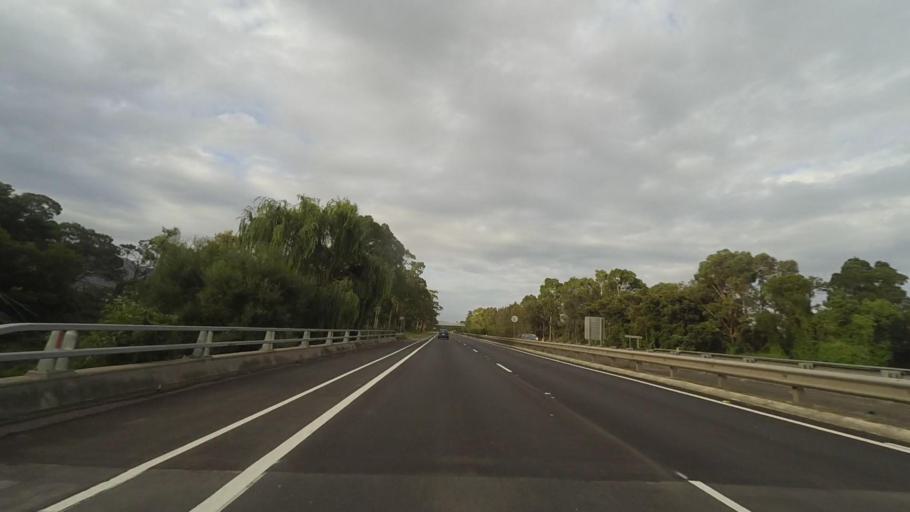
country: AU
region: New South Wales
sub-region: Wollongong
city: Fairy Meadow
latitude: -34.3985
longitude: 150.8943
